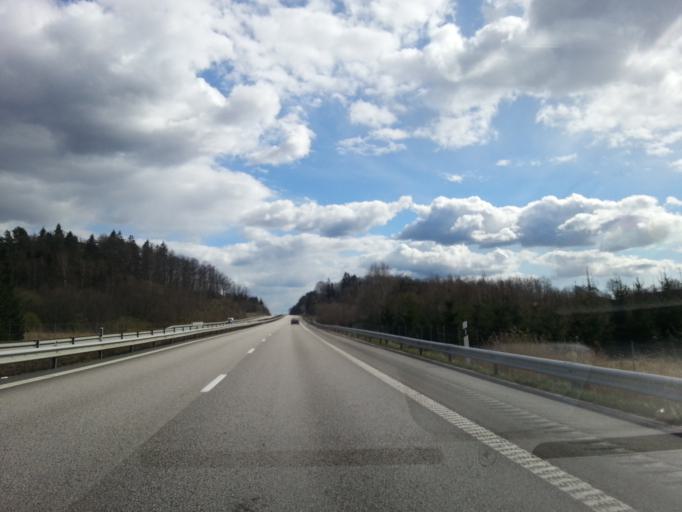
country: SE
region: Vaestra Goetaland
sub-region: Uddevalla Kommun
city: Ljungskile
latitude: 58.2632
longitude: 11.8964
